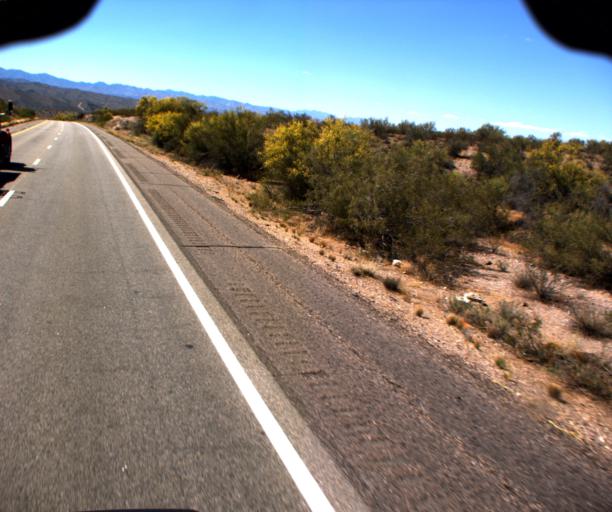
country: US
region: Arizona
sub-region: Yavapai County
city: Bagdad
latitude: 34.6285
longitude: -113.5400
